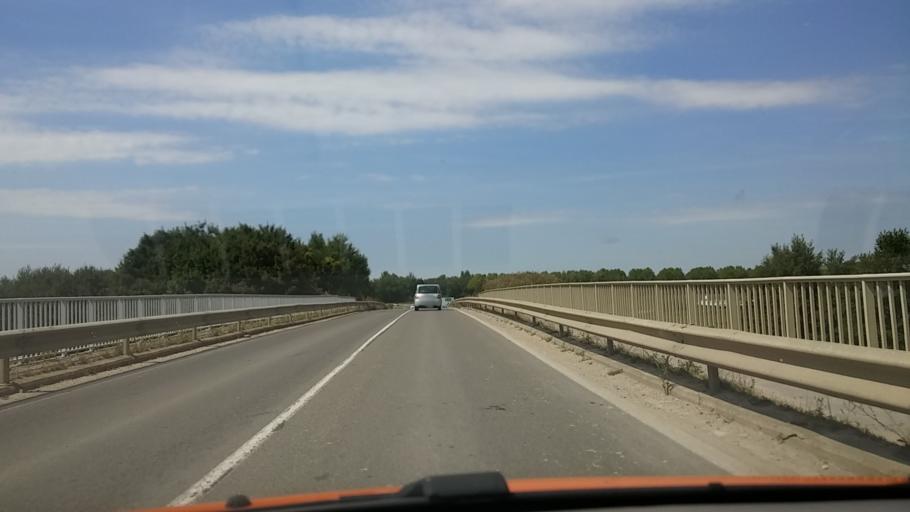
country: FR
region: Ile-de-France
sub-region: Departement de Seine-et-Marne
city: Serris
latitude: 48.8333
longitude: 2.7961
